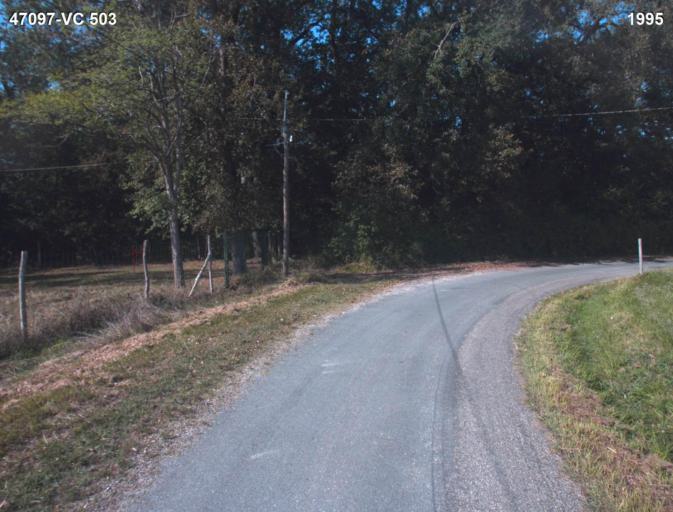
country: FR
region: Aquitaine
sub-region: Departement du Lot-et-Garonne
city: Port-Sainte-Marie
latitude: 44.2079
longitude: 0.3691
